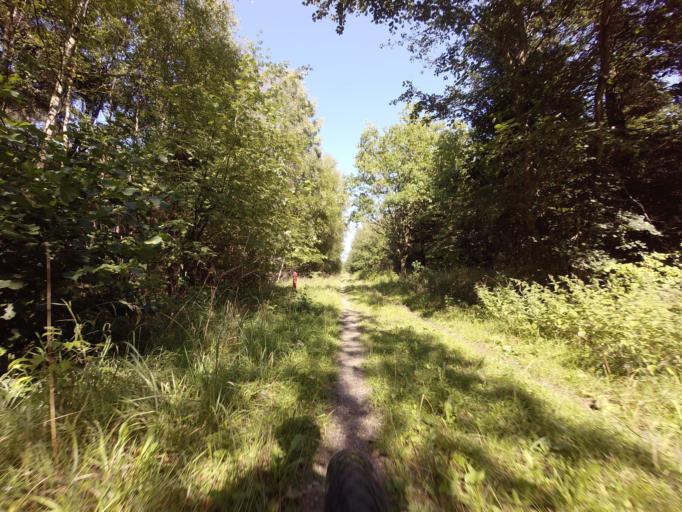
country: DK
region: North Denmark
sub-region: Hjorring Kommune
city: Hirtshals
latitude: 57.5777
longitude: 10.0019
